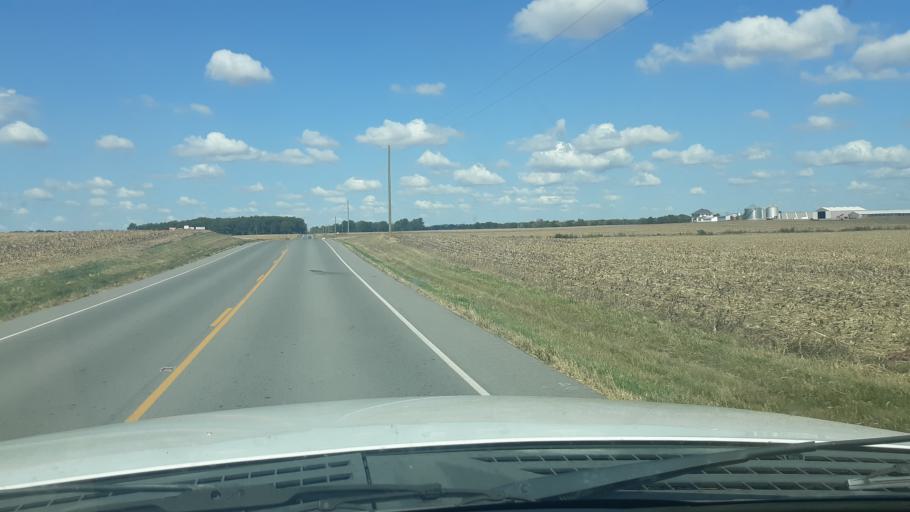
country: US
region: Illinois
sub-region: Saline County
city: Eldorado
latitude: 37.7993
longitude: -88.4848
